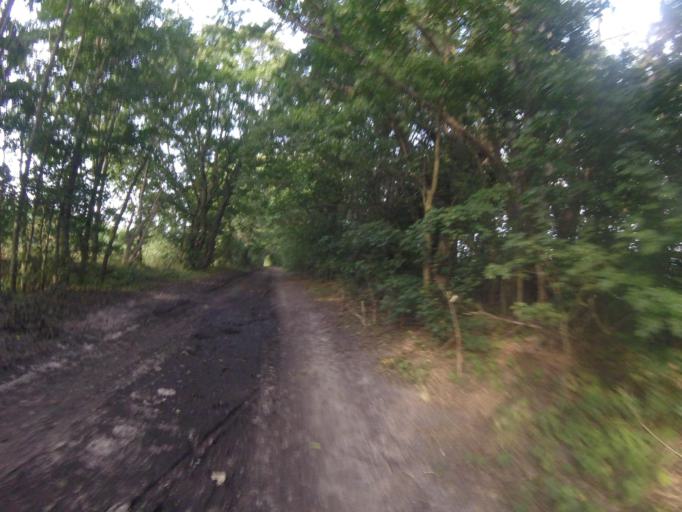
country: DE
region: Berlin
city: Gropiusstadt
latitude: 52.3951
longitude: 13.4675
